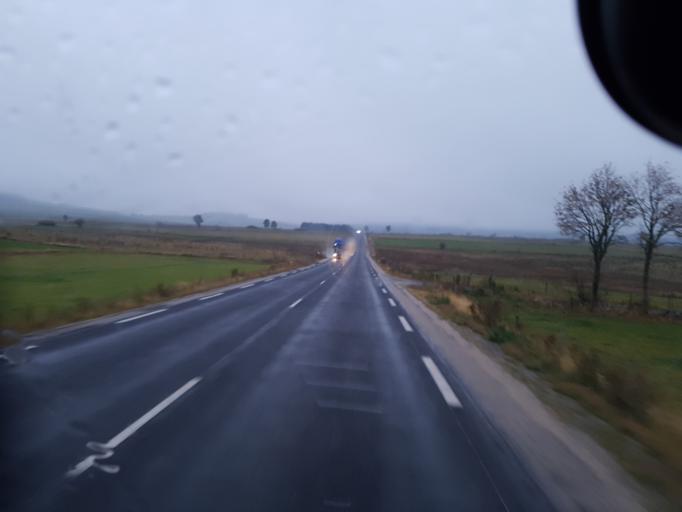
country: FR
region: Languedoc-Roussillon
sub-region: Departement de la Lozere
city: Langogne
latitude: 44.8159
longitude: 3.8748
